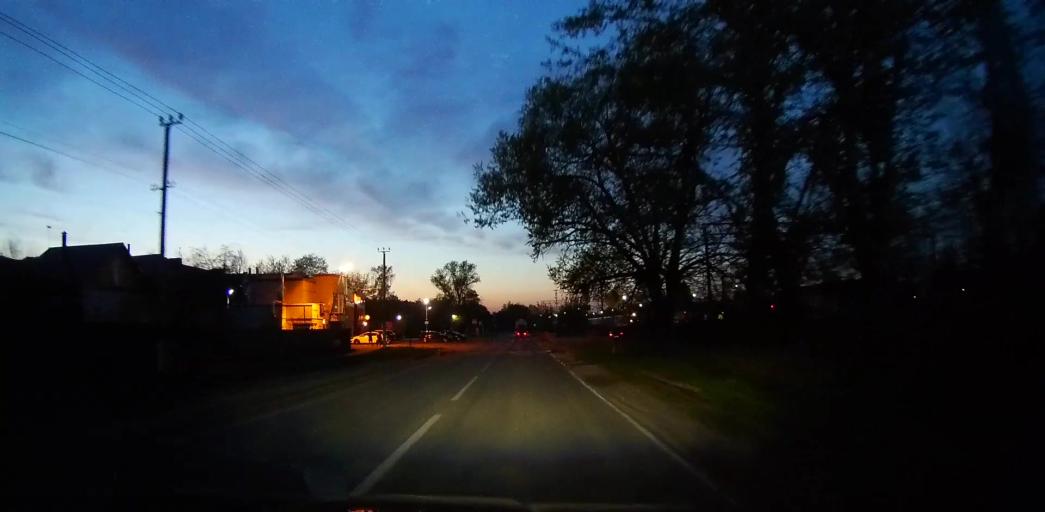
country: RU
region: Moskovskaya
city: Peski
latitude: 55.2139
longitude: 38.7717
